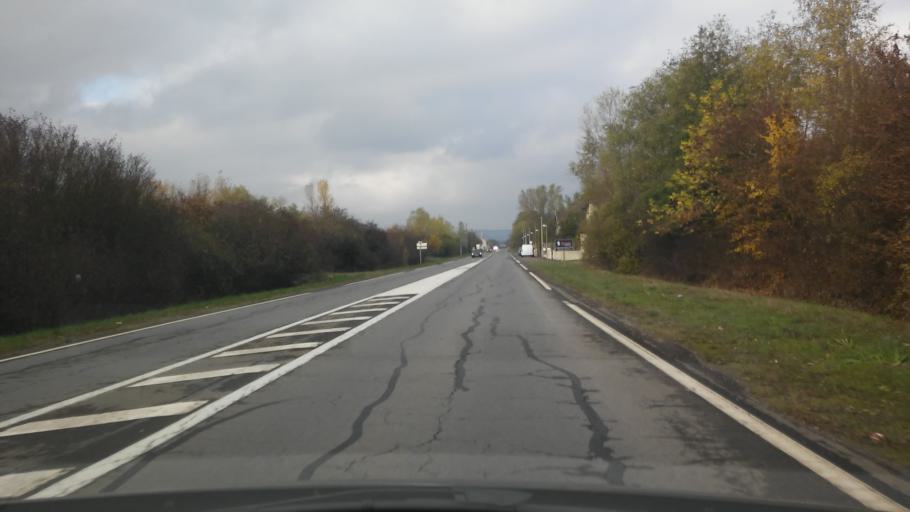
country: FR
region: Lorraine
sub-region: Departement de la Moselle
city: Uckange
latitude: 49.3146
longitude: 6.1575
